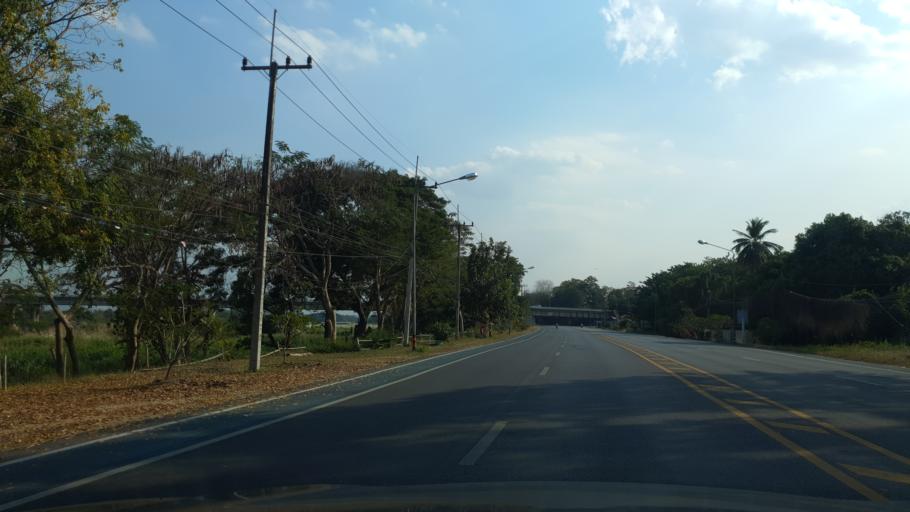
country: TH
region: Tak
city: Tak
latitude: 16.8583
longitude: 99.1218
